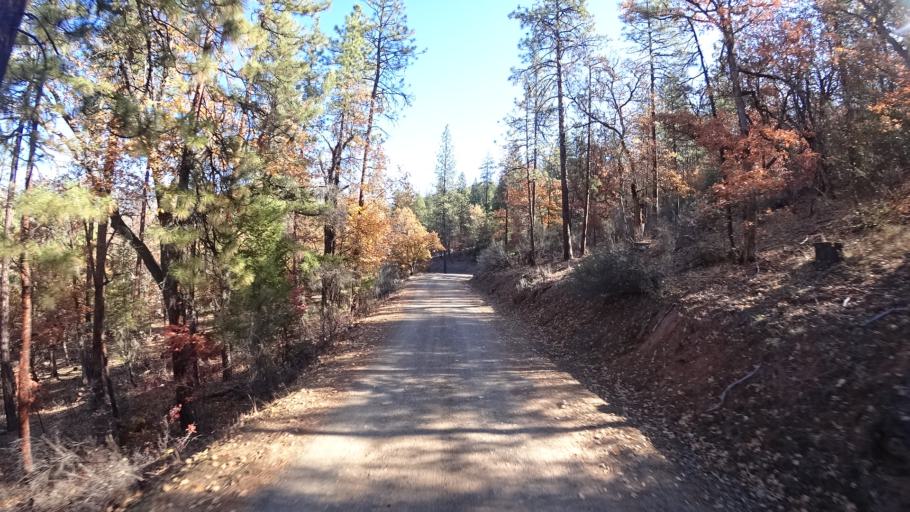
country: US
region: California
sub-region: Siskiyou County
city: Yreka
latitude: 41.8558
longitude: -122.8290
